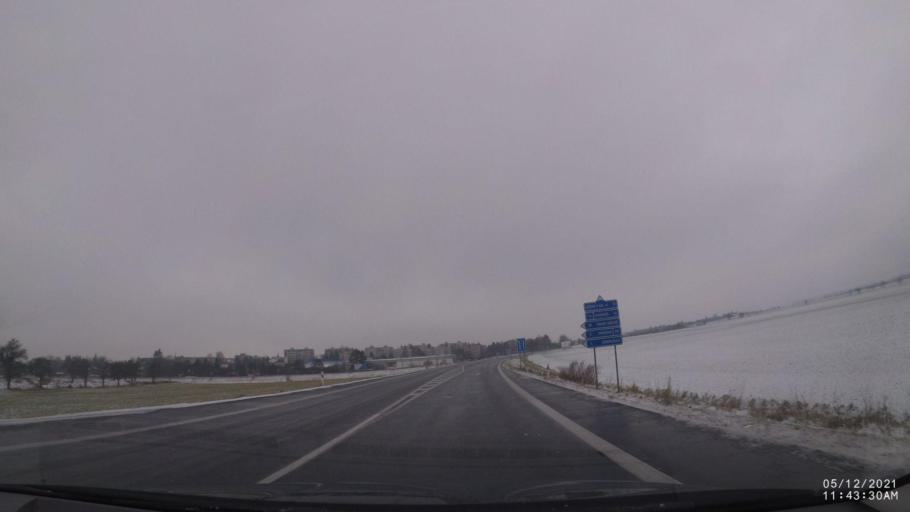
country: CZ
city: Dobruska
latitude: 50.2869
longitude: 16.1710
